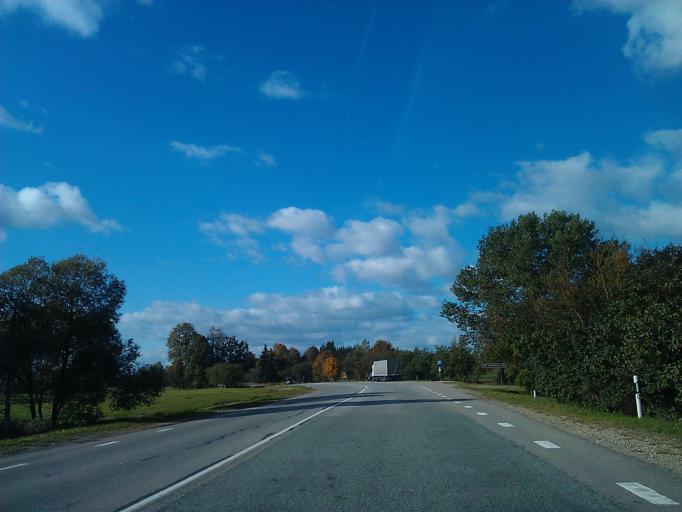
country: LV
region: Jekabpils Rajons
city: Jekabpils
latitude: 56.4910
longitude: 25.9164
